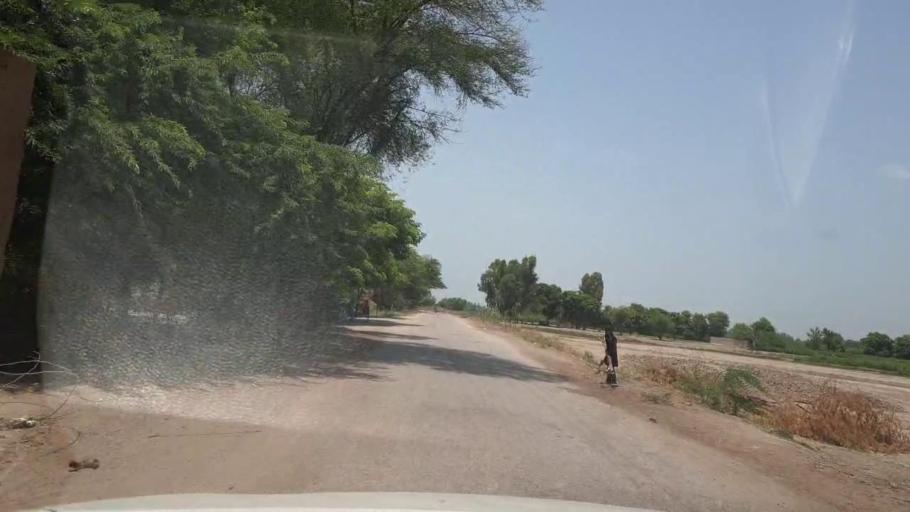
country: PK
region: Sindh
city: Bozdar
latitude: 27.1867
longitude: 68.6194
